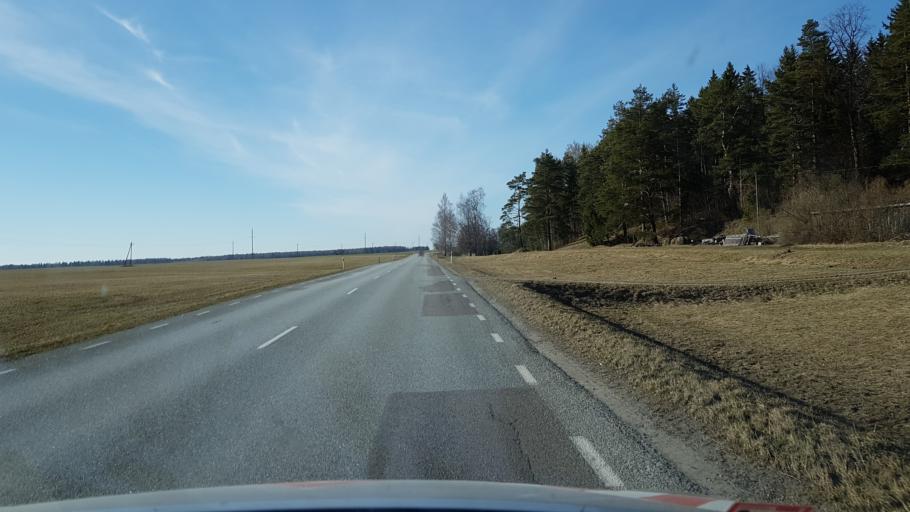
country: EE
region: Laeaene-Virumaa
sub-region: Vinni vald
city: Vinni
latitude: 59.1934
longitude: 26.5680
